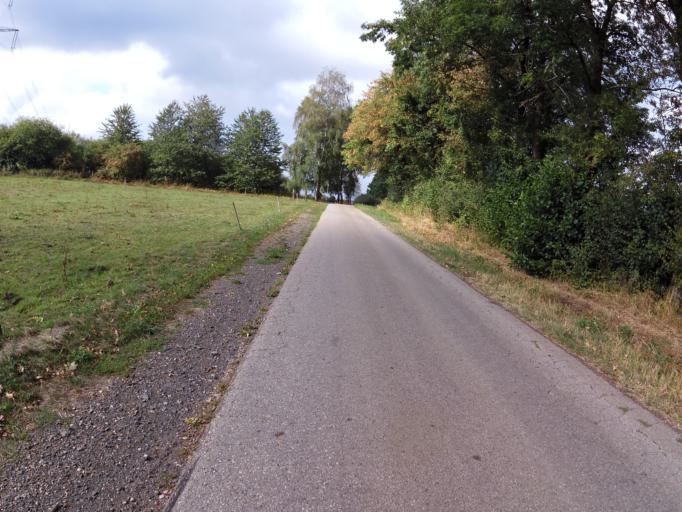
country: DE
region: North Rhine-Westphalia
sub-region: Regierungsbezirk Koln
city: Dahlem
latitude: 50.4168
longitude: 6.5753
